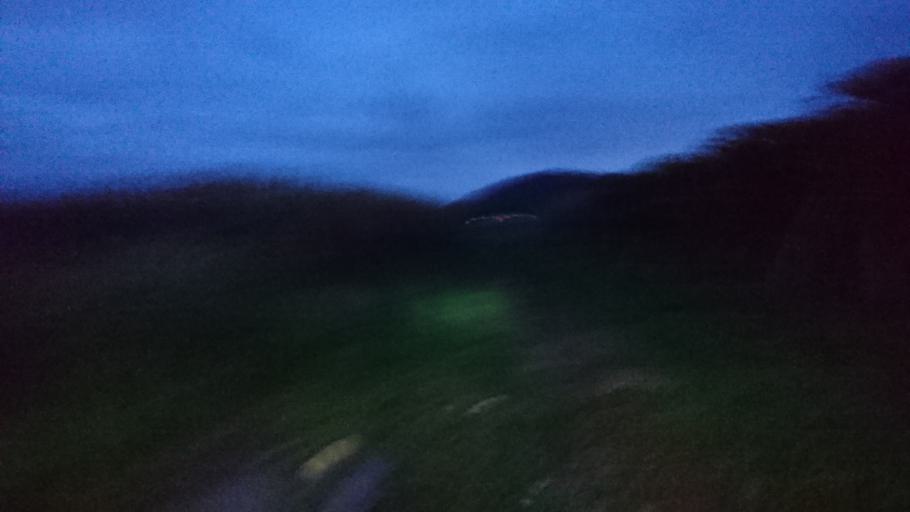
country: IT
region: Veneto
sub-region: Provincia di Treviso
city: Covolo-Levada
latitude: 45.8491
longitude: 12.0142
